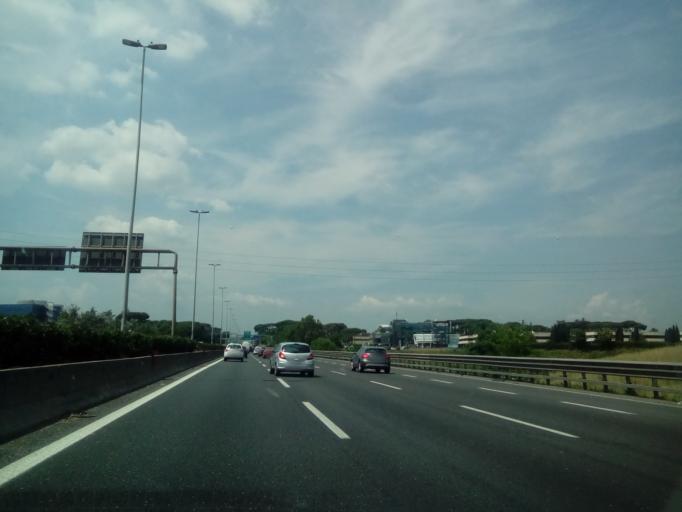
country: IT
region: Latium
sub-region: Citta metropolitana di Roma Capitale
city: Setteville
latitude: 41.9247
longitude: 12.6082
